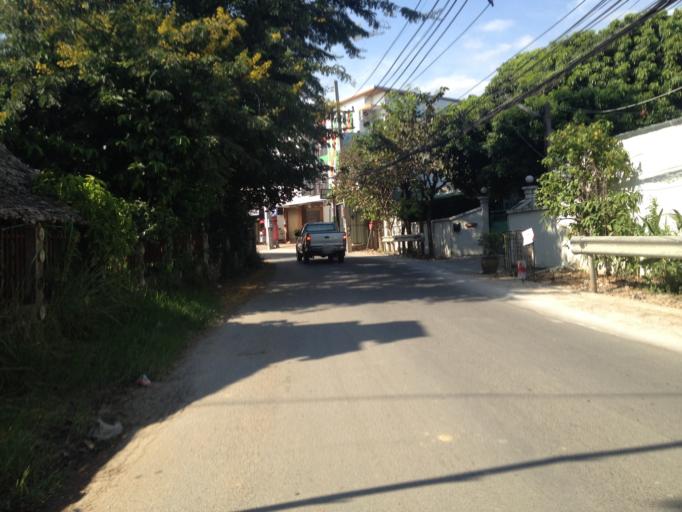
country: TH
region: Chiang Mai
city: Chiang Mai
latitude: 18.7643
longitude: 98.9762
